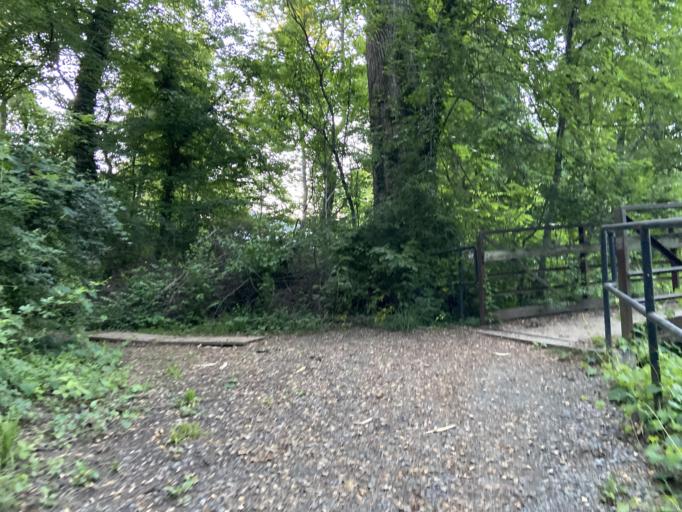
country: US
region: Virginia
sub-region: Fairfax County
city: McLean
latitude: 38.9219
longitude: -77.1740
